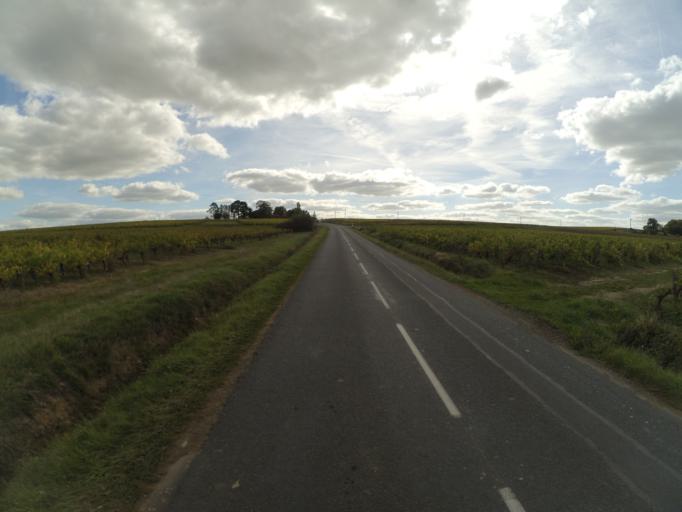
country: FR
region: Pays de la Loire
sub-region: Departement de la Loire-Atlantique
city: Le Loroux-Bottereau
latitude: 47.2186
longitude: -1.3594
